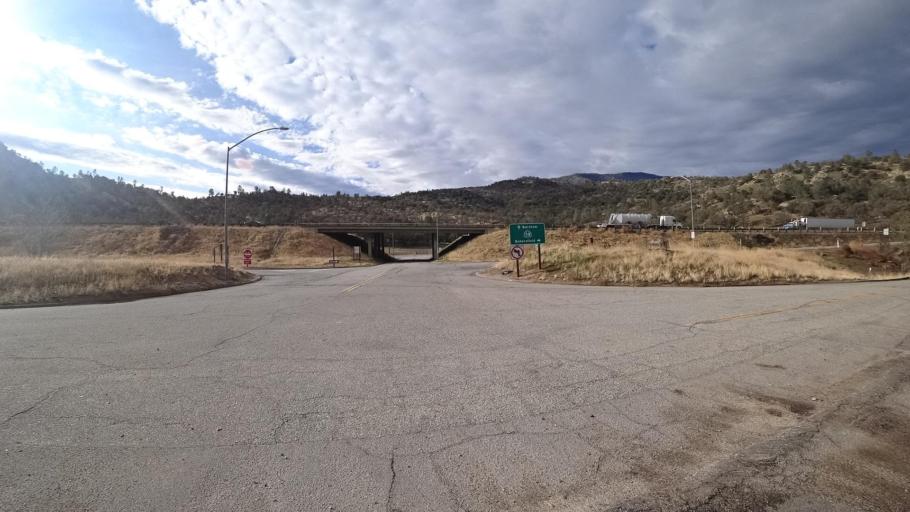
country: US
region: California
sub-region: Kern County
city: Bear Valley Springs
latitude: 35.2242
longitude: -118.5664
